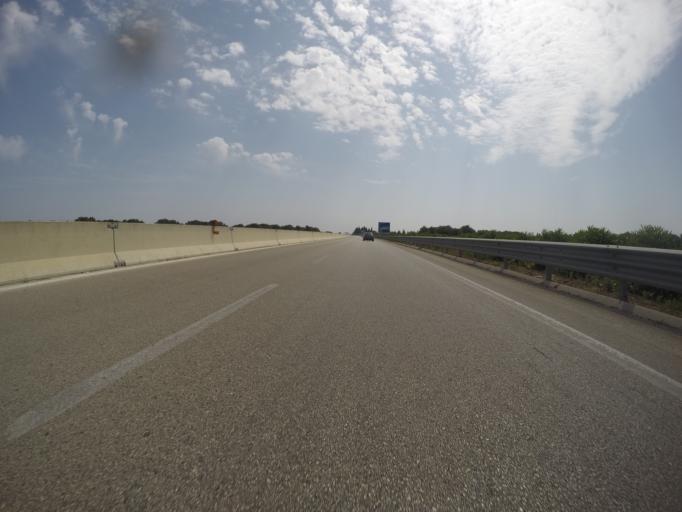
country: IT
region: Apulia
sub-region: Provincia di Brindisi
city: Mesagne
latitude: 40.5657
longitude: 17.7764
